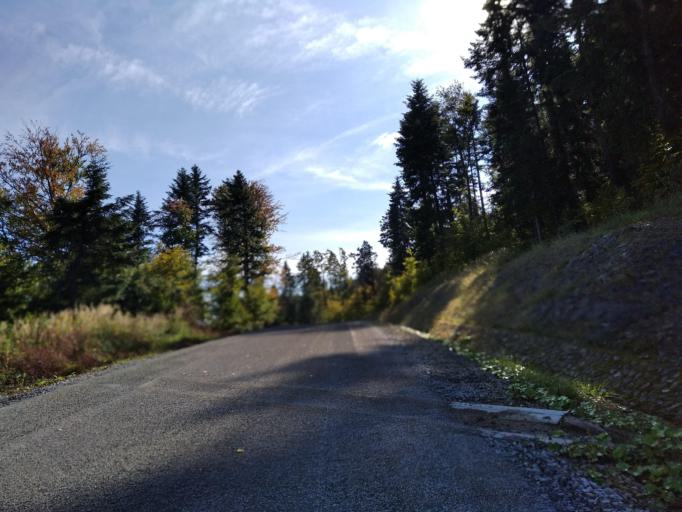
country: PL
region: Subcarpathian Voivodeship
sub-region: Powiat strzyzowski
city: Strzyzow
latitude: 49.8198
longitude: 21.8057
